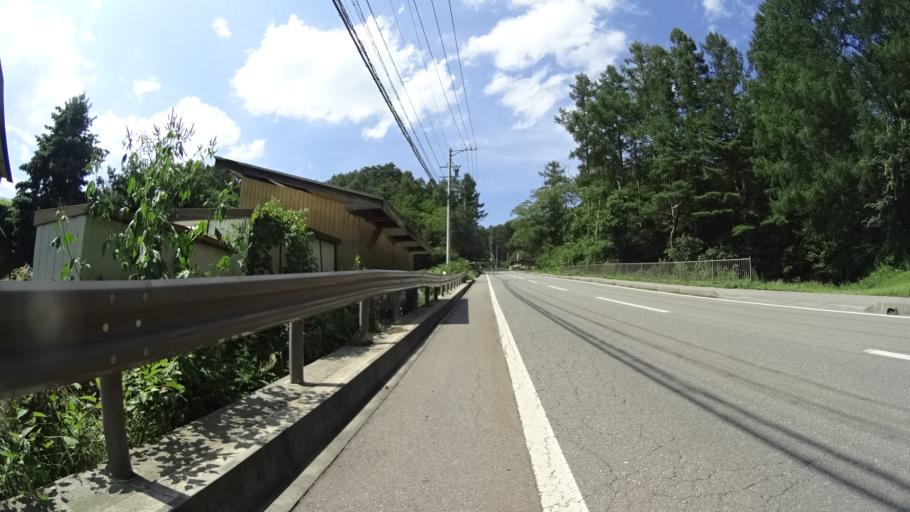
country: JP
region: Nagano
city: Saku
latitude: 36.0525
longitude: 138.4521
